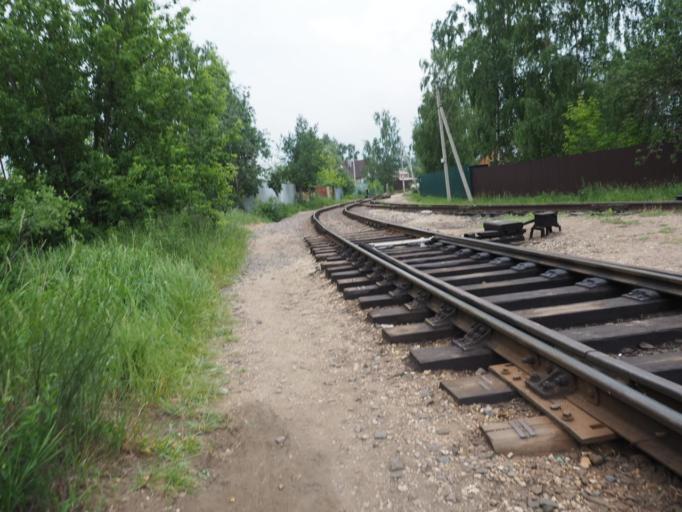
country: RU
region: Moskovskaya
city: Lyubertsy
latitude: 55.6517
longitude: 37.8948
